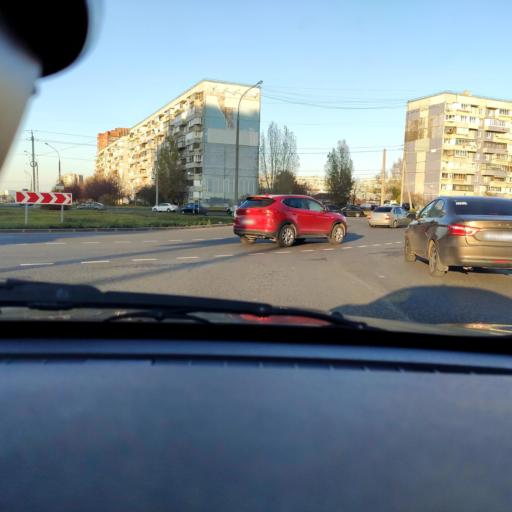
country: RU
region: Samara
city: Tol'yatti
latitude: 53.5419
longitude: 49.3308
